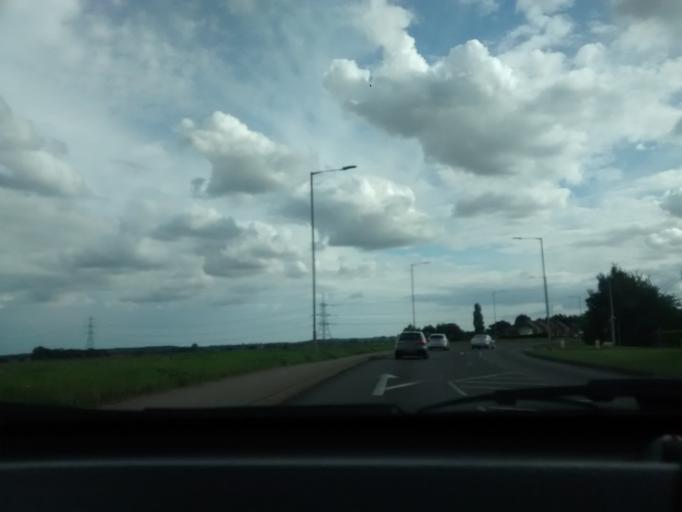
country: GB
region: England
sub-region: Norfolk
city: King's Lynn
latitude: 52.7075
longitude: 0.4177
